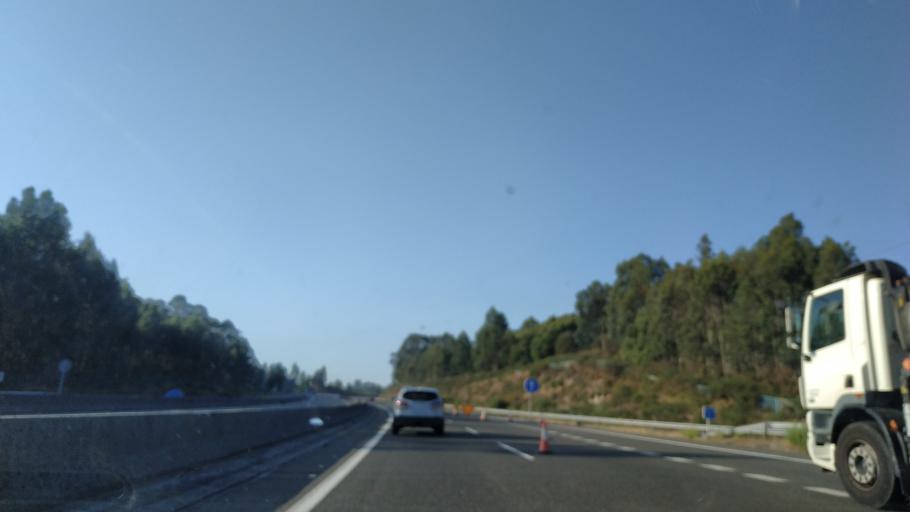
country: ES
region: Galicia
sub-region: Provincia da Coruna
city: Arteixo
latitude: 43.3044
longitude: -8.4755
